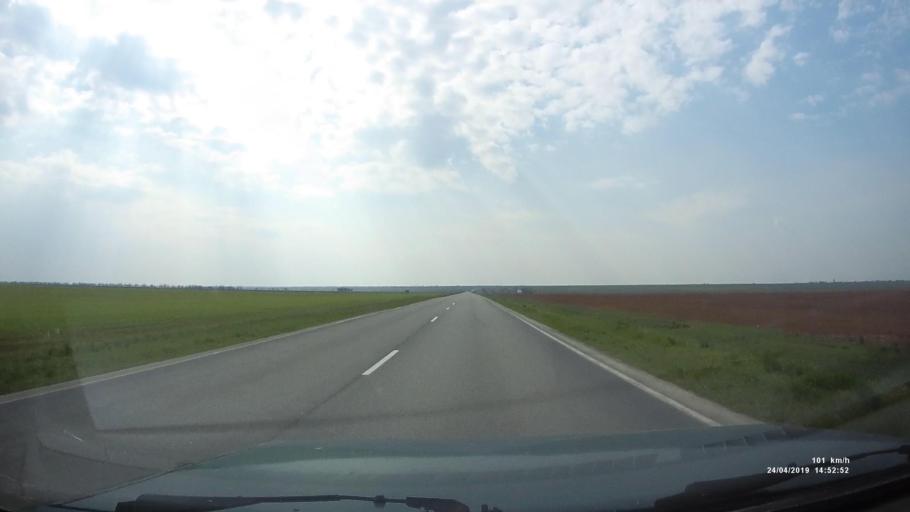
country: RU
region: Rostov
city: Remontnoye
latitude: 46.5307
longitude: 43.6714
